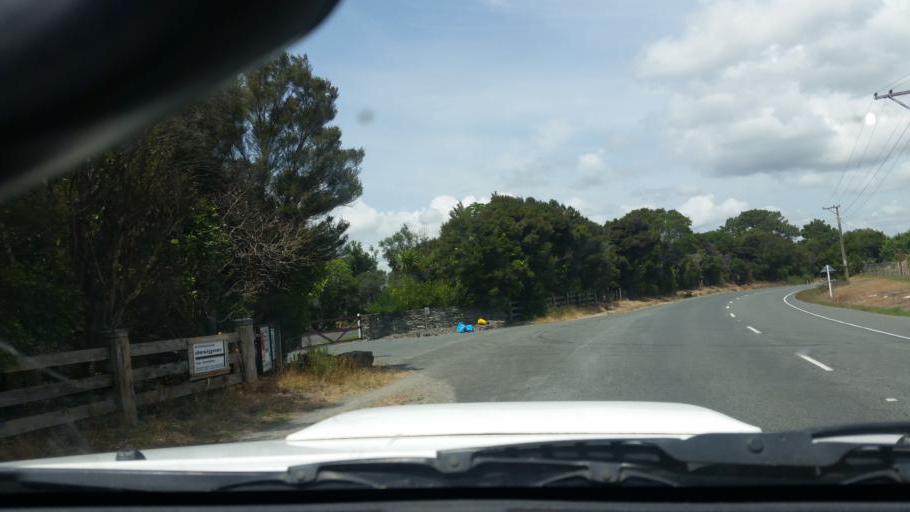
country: NZ
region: Auckland
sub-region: Auckland
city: Wellsford
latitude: -36.1153
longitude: 174.5751
